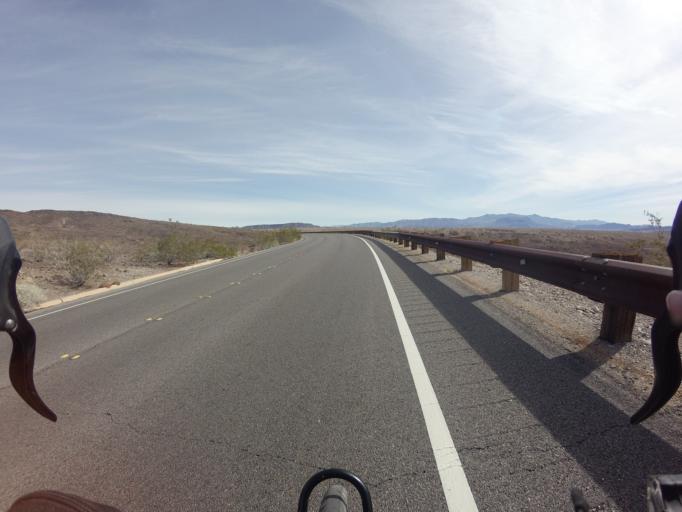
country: US
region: Nevada
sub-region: Clark County
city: Henderson
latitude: 36.1448
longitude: -114.8594
